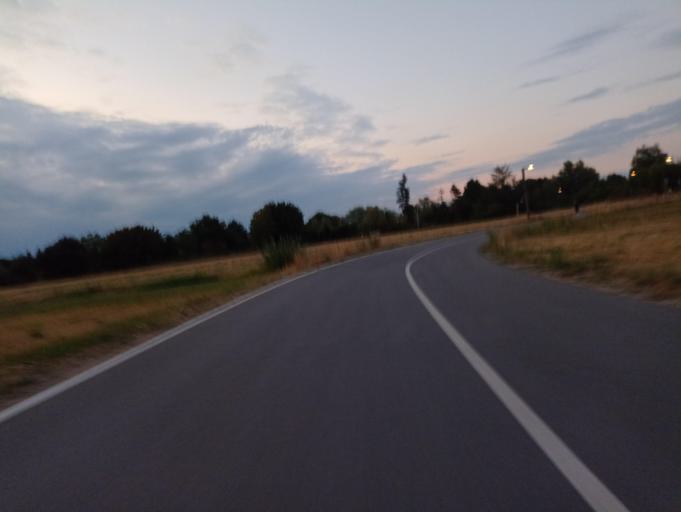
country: DE
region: Hesse
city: Langen
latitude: 49.9796
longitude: 8.6577
